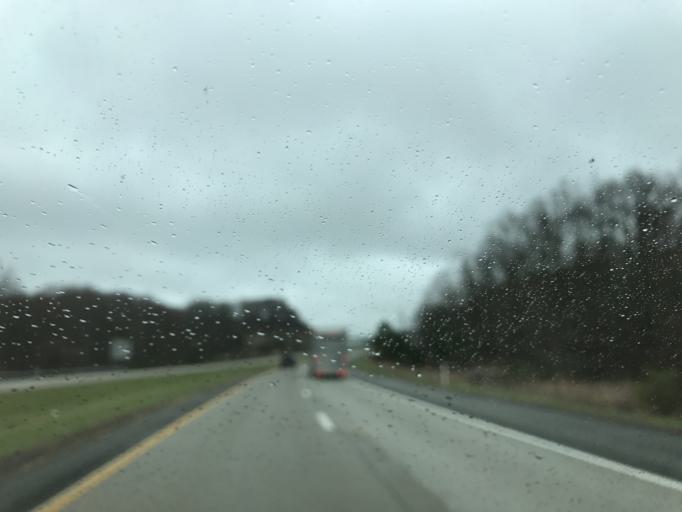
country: US
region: West Virginia
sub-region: Greenbrier County
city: Rainelle
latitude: 37.8655
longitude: -80.7083
